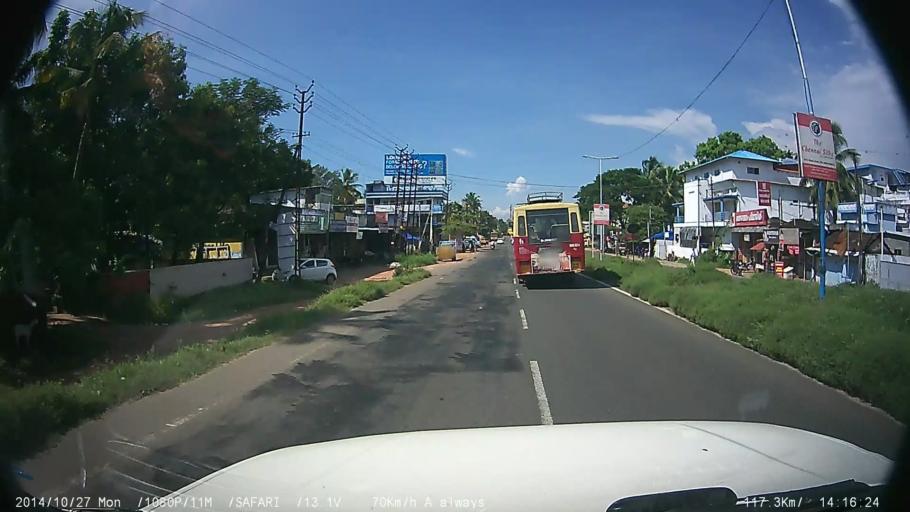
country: IN
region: Kerala
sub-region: Alappuzha
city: Arukutti
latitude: 9.8426
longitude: 76.3085
